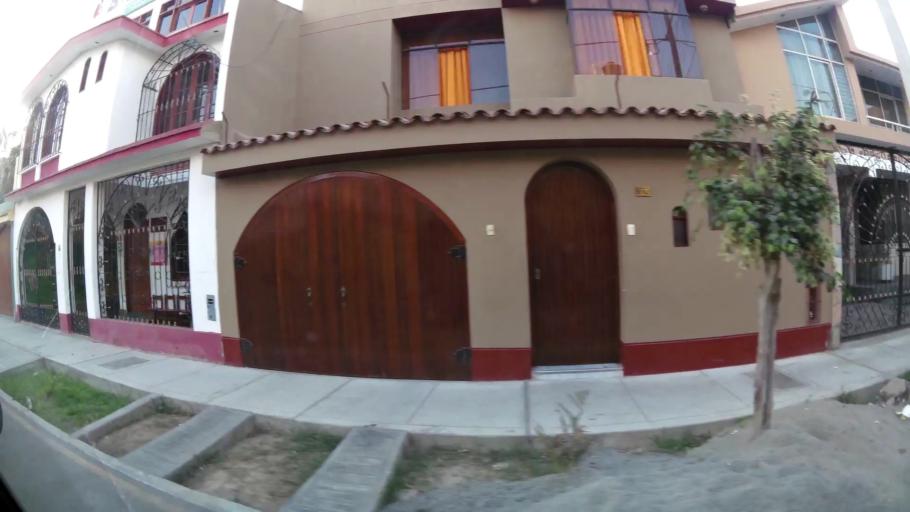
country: PE
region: Ica
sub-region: Provincia de Ica
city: Ica
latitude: -14.0805
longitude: -75.7272
